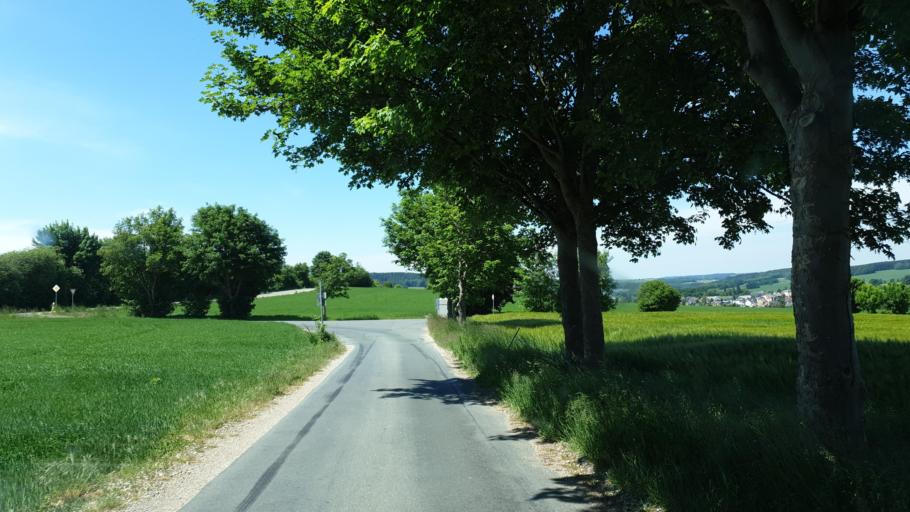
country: DE
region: Saxony
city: Rodewisch
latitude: 50.5232
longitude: 12.4237
